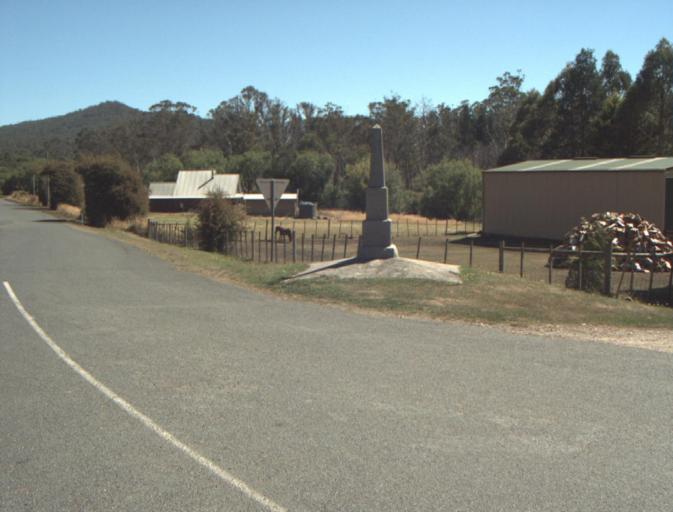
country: AU
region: Tasmania
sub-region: Launceston
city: Newstead
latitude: -41.3908
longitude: 147.2977
